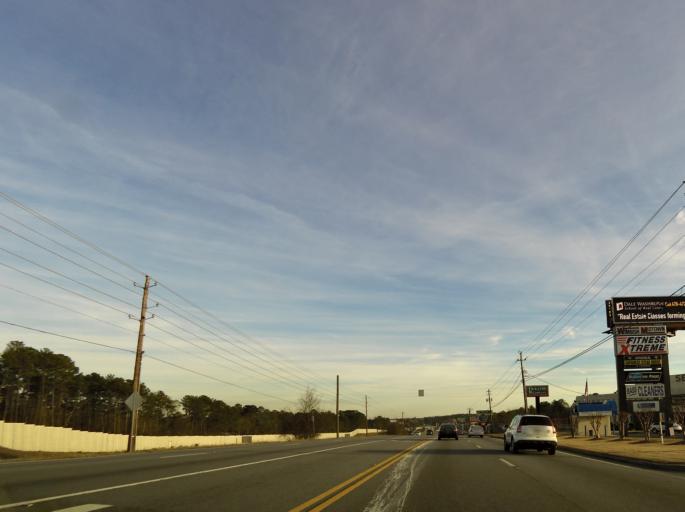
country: US
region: Georgia
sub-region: Bibb County
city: Macon
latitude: 32.8859
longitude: -83.6731
